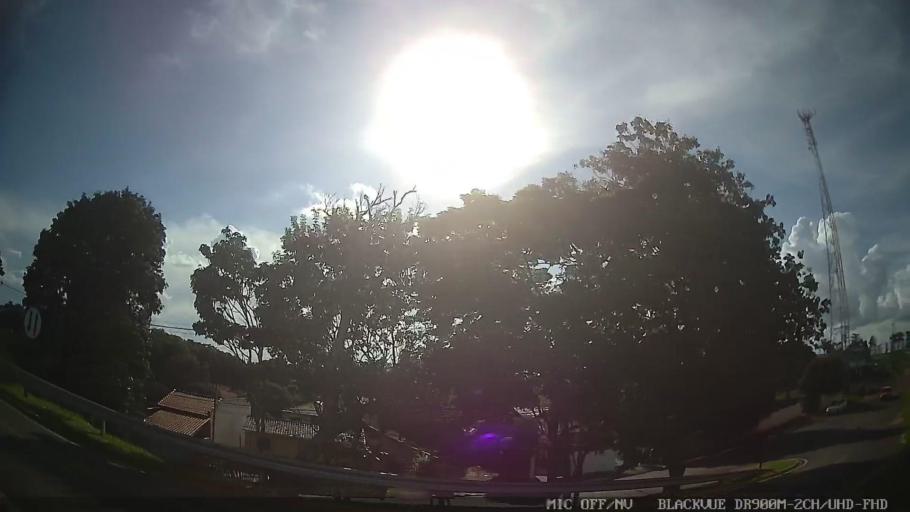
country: BR
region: Sao Paulo
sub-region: Laranjal Paulista
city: Laranjal Paulista
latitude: -23.0810
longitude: -47.7913
